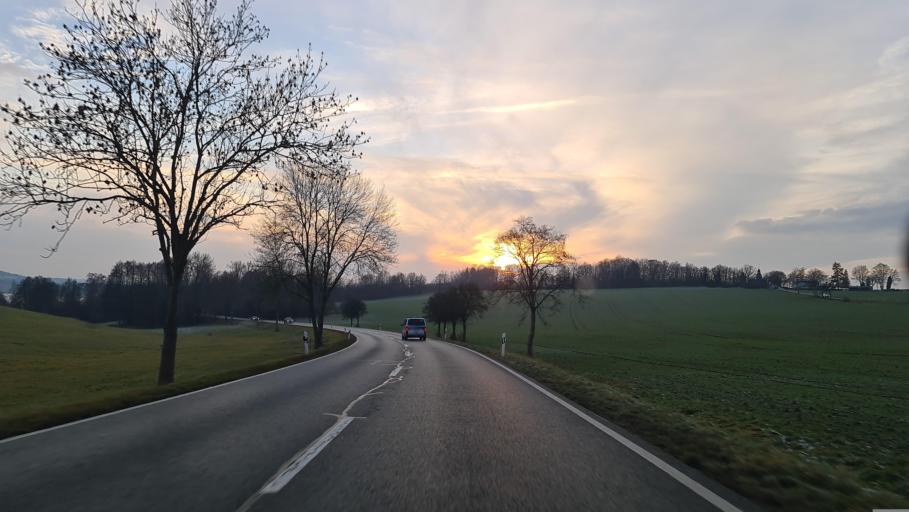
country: DE
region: Saxony
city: Pohl
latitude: 50.5605
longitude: 12.1953
